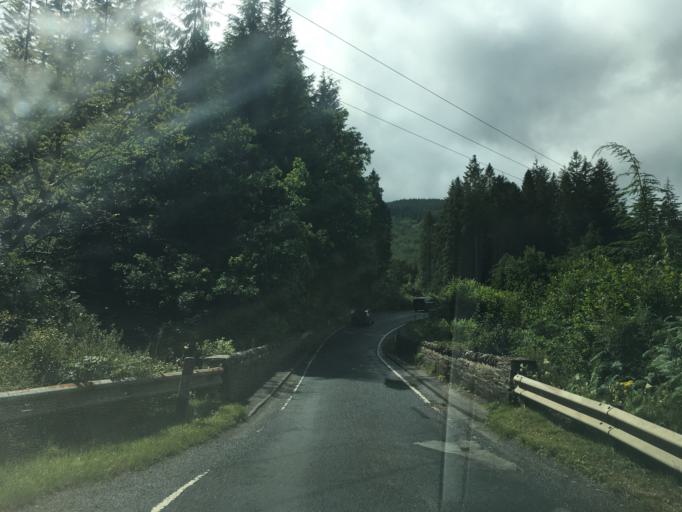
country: GB
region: Scotland
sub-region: Argyll and Bute
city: Dunoon
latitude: 55.9894
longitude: -4.9939
